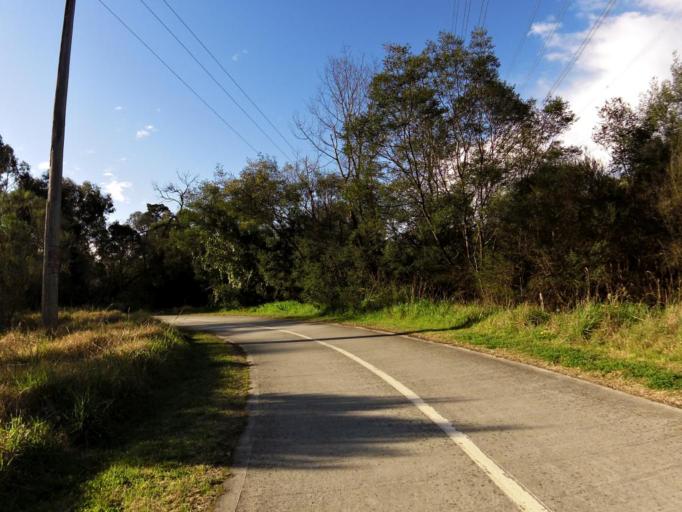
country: AU
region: Victoria
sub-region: Knox
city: Wantirna
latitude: -37.8472
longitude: 145.2123
